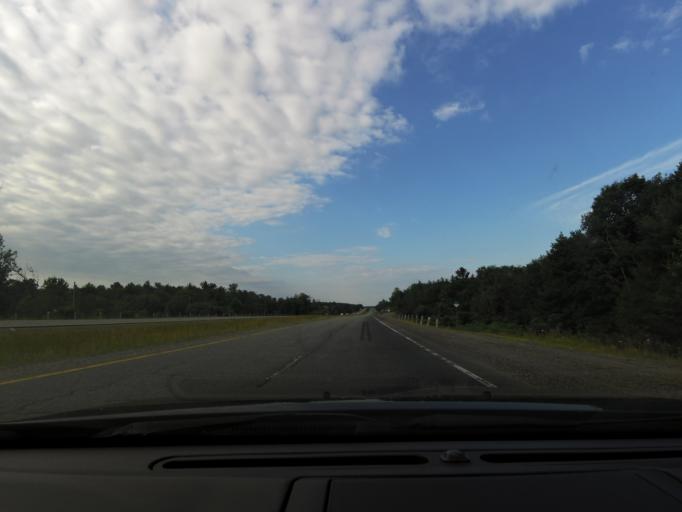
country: CA
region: Ontario
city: Gravenhurst
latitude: 44.9616
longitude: -79.3258
